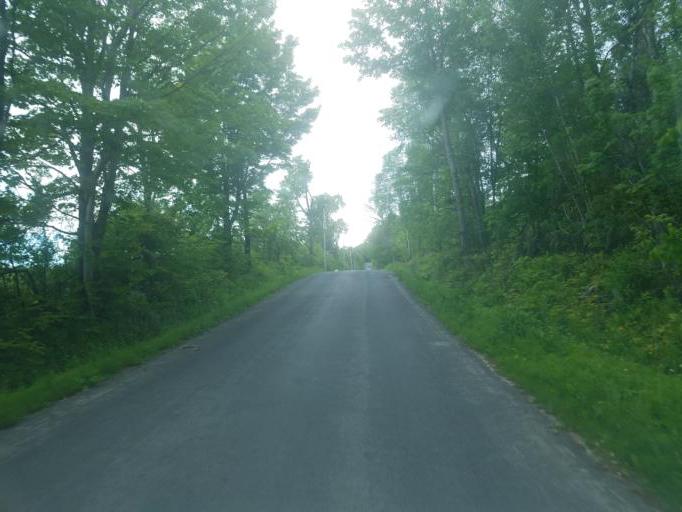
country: US
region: New York
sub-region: Herkimer County
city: Herkimer
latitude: 43.2174
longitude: -74.9540
